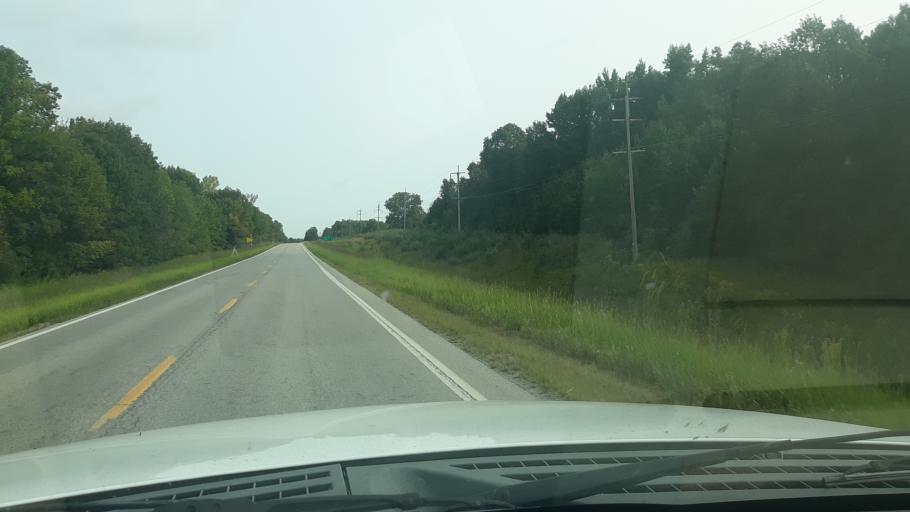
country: US
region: Illinois
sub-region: White County
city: Norris City
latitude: 37.9095
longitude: -88.3567
